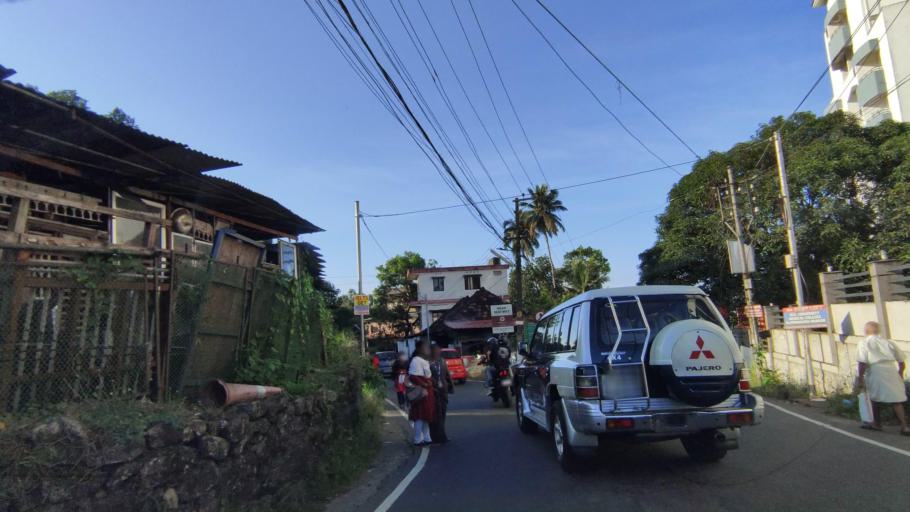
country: IN
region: Kerala
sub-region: Kottayam
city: Kottayam
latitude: 9.5953
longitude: 76.5168
